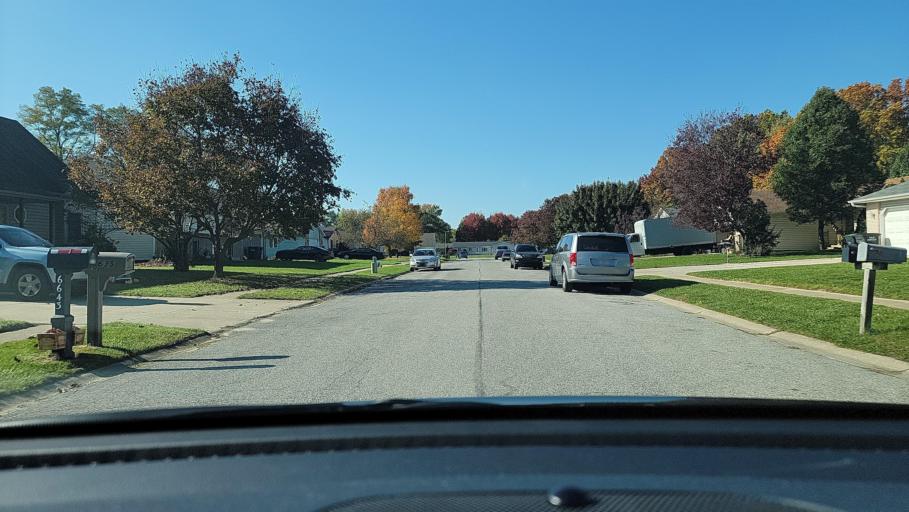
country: US
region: Indiana
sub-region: Porter County
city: Portage
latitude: 41.5808
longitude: -87.1585
